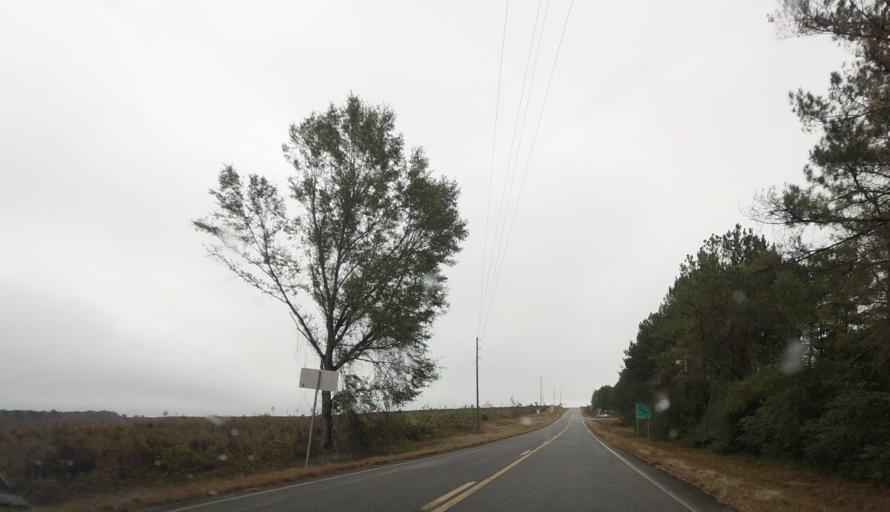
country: US
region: Georgia
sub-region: Taylor County
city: Butler
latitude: 32.4447
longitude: -84.3676
